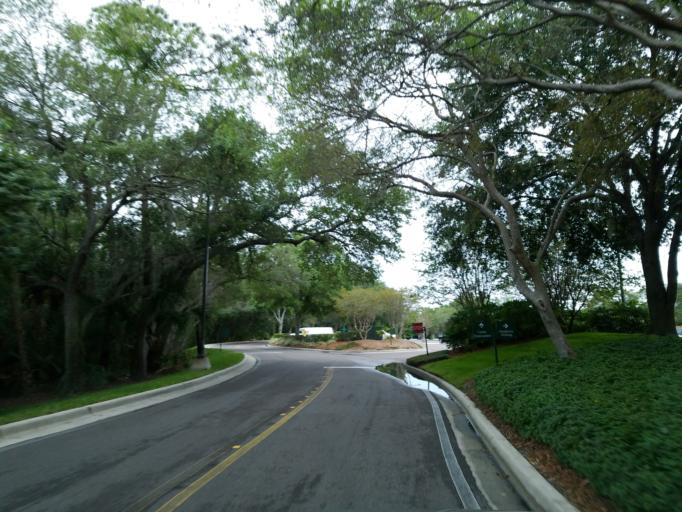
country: US
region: Florida
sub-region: Hillsborough County
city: Town 'n' Country
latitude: 27.9650
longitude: -82.5487
